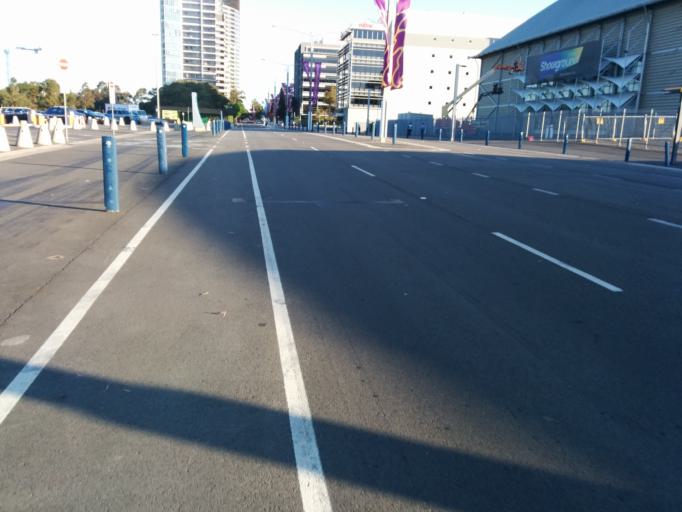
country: AU
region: New South Wales
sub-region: Canada Bay
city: Concord West
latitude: -33.8439
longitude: 151.0709
